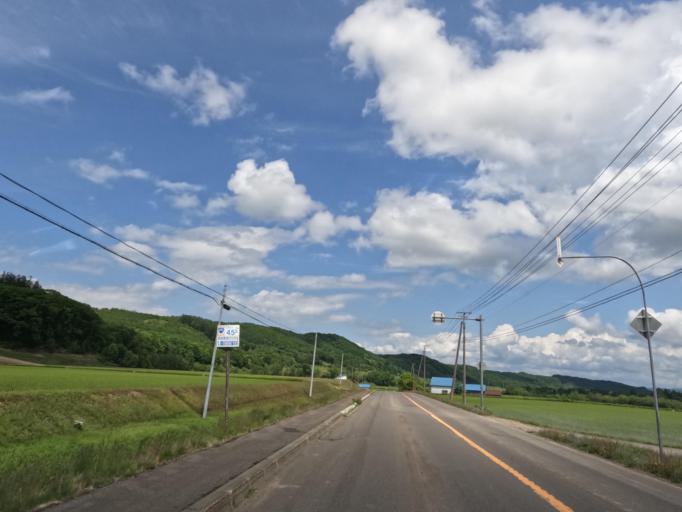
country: JP
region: Hokkaido
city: Takikawa
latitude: 43.5843
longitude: 141.7937
